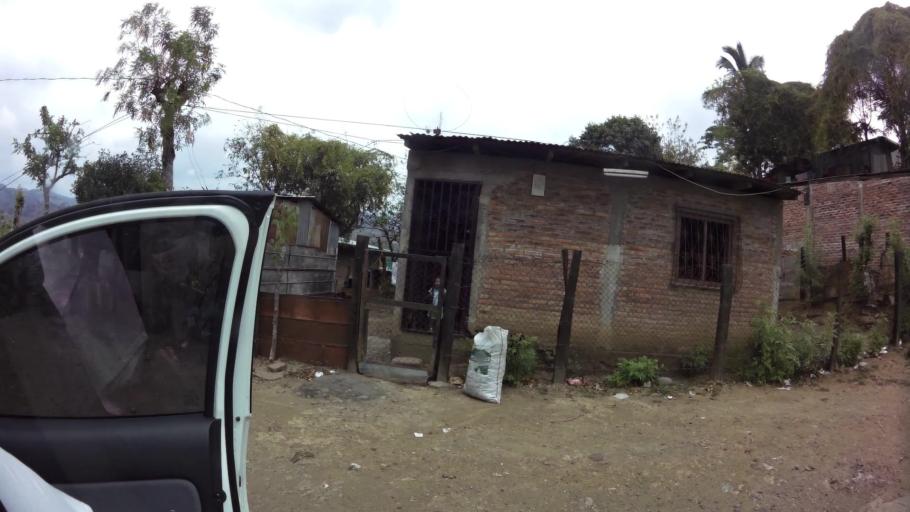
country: NI
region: Matagalpa
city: Matagalpa
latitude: 12.9317
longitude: -85.9162
